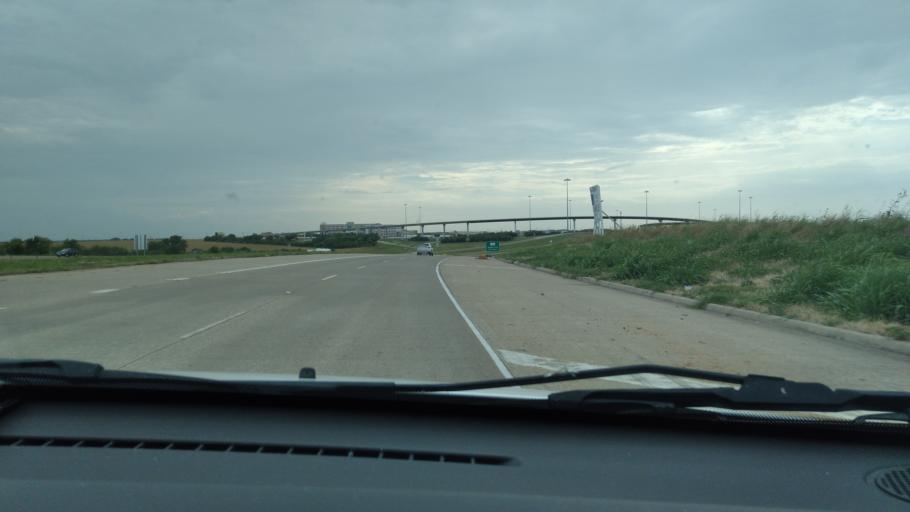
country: US
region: Texas
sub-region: McLennan County
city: Beverly Hills
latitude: 31.4913
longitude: -97.1426
